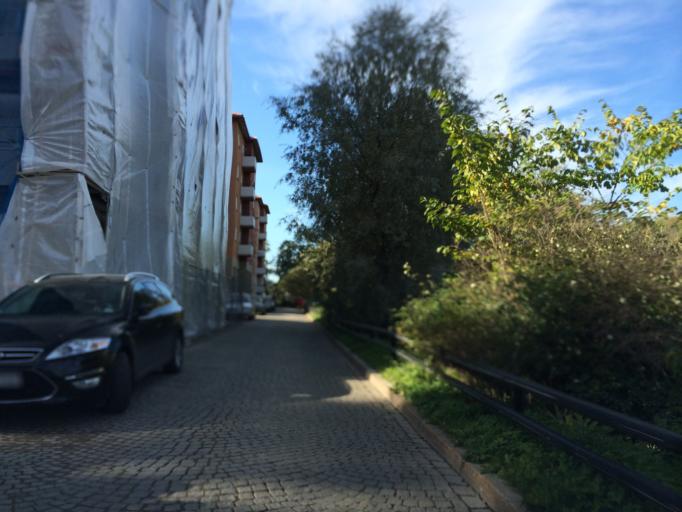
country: SE
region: Stockholm
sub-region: Stockholms Kommun
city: Arsta
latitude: 59.3197
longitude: 18.0234
